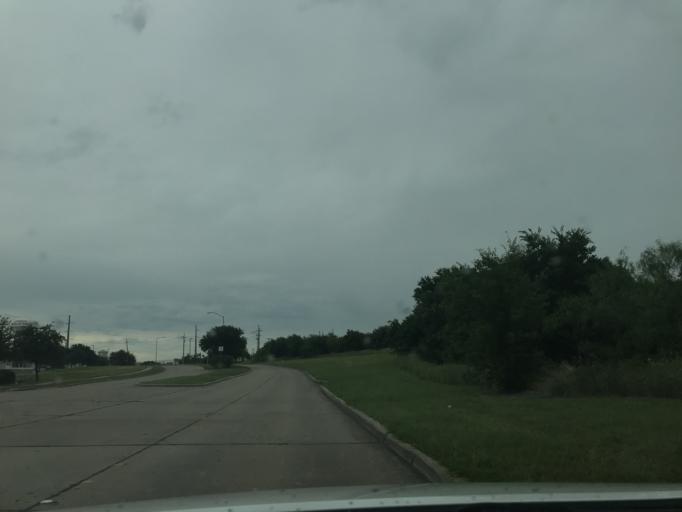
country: US
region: Texas
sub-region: Denton County
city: Lewisville
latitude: 33.0507
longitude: -97.0131
